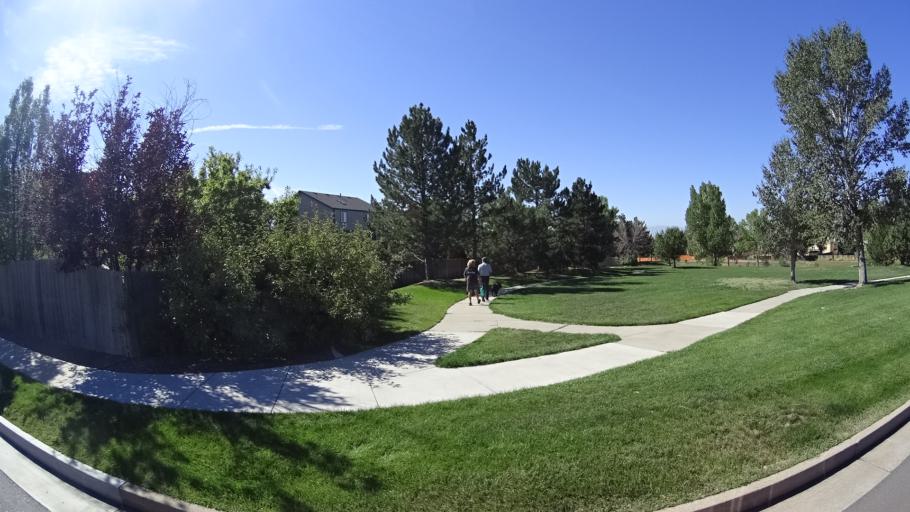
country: US
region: Colorado
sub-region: El Paso County
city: Black Forest
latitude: 38.9531
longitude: -104.7276
